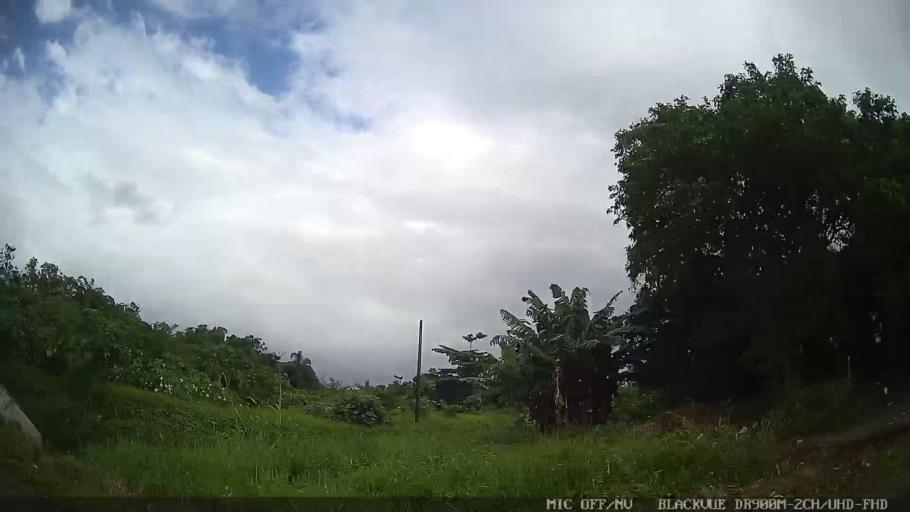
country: BR
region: Sao Paulo
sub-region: Itanhaem
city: Itanhaem
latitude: -24.1859
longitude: -46.8140
